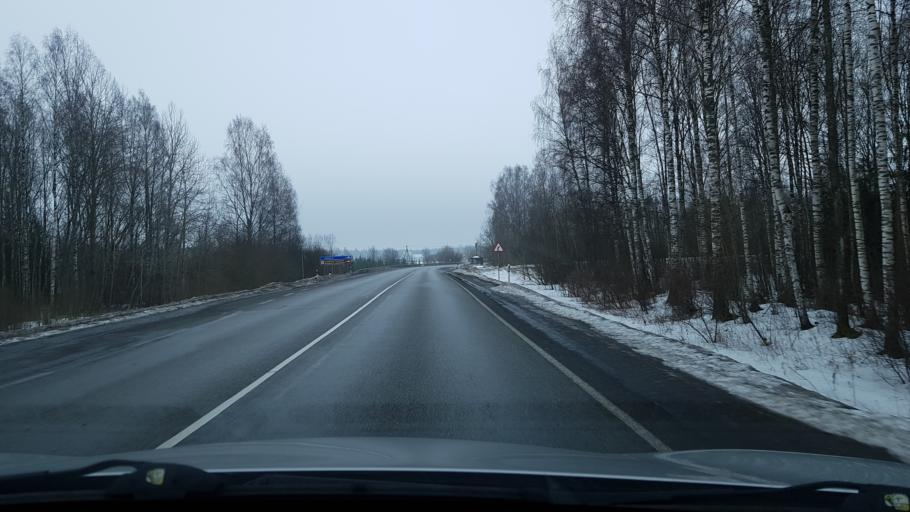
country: EE
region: Valgamaa
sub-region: Valga linn
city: Valga
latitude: 57.9106
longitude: 26.1827
